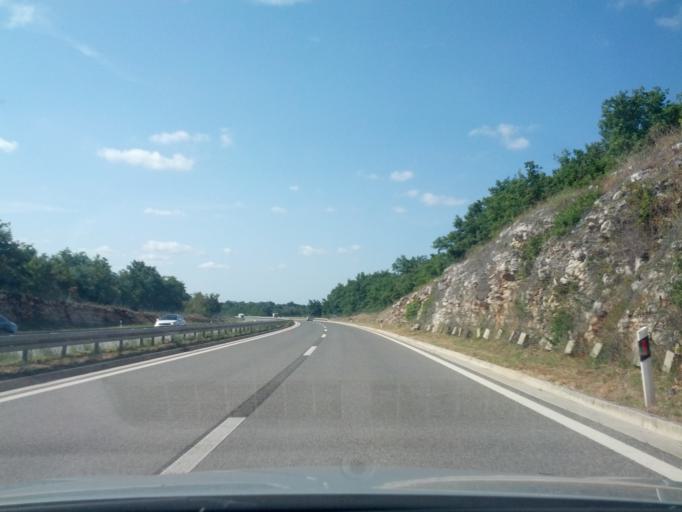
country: HR
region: Istarska
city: Buje
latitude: 45.3870
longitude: 13.6163
